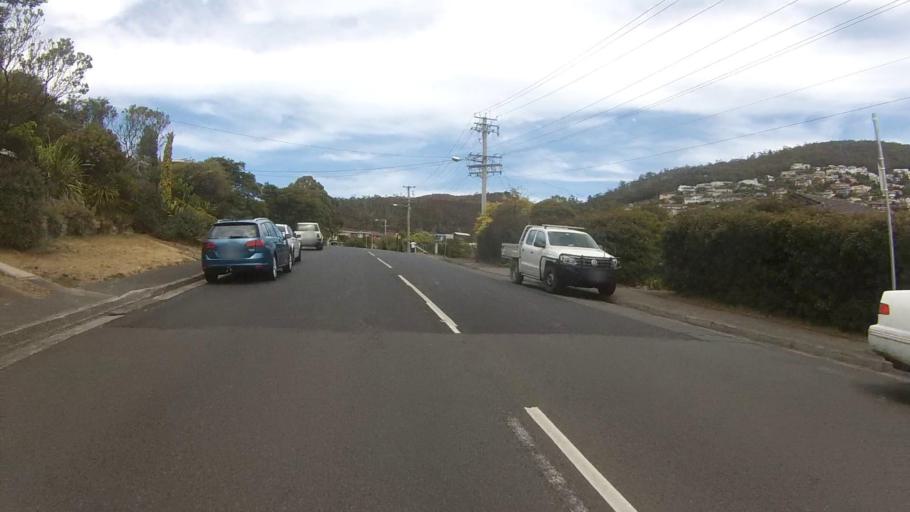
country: AU
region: Tasmania
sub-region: Kingborough
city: Taroona
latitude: -42.9167
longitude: 147.3555
